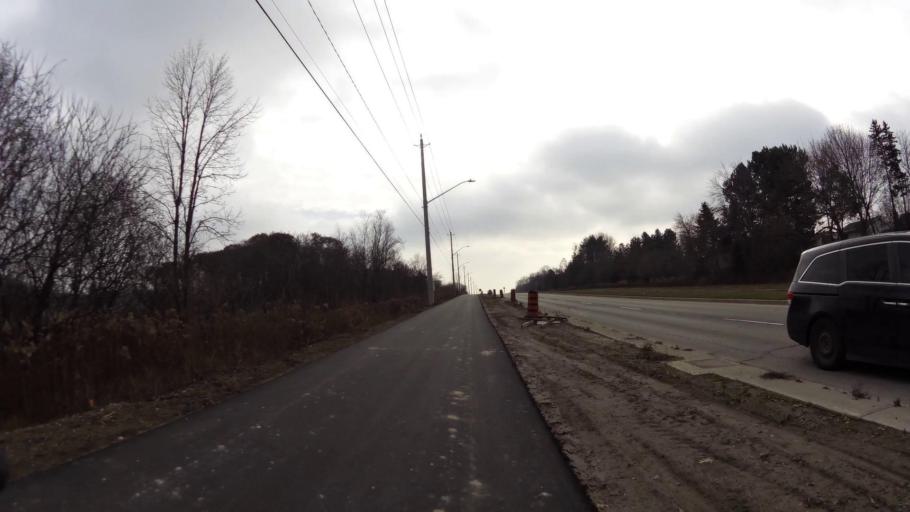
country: CA
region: Ontario
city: Kitchener
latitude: 43.4136
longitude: -80.4651
